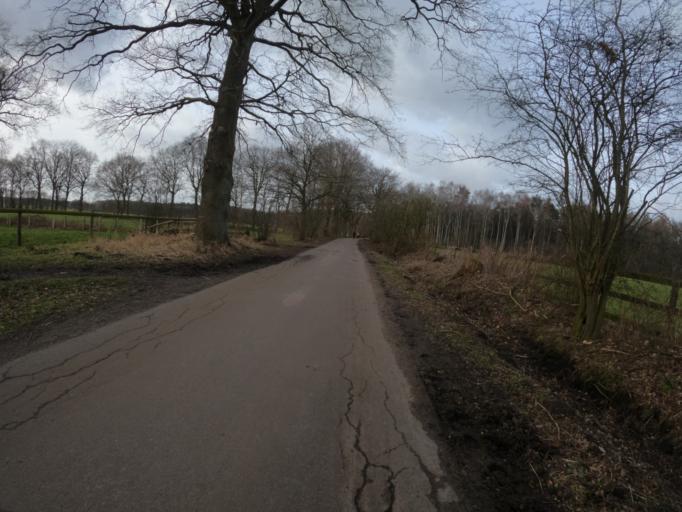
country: DE
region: Schleswig-Holstein
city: Rellingen
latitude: 53.6031
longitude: 9.7903
